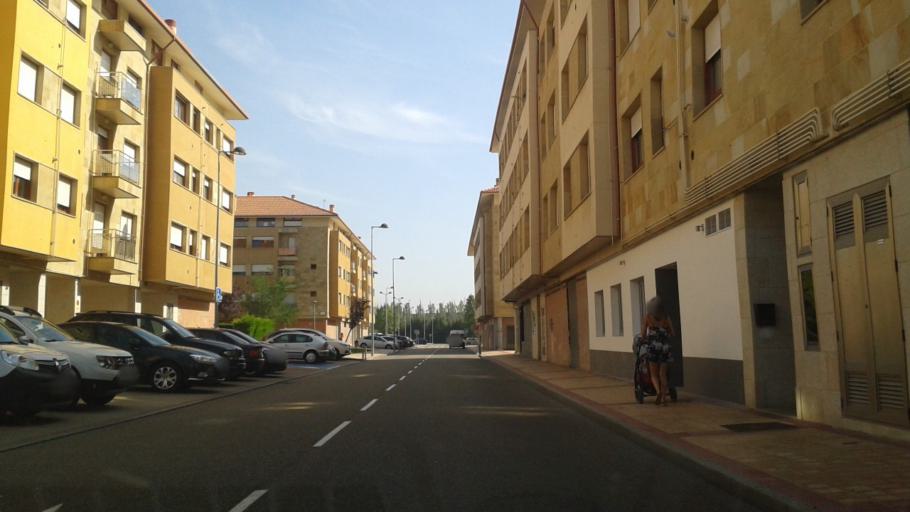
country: ES
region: Castille and Leon
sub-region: Provincia de Valladolid
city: Arroyo
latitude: 41.6197
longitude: -4.7771
